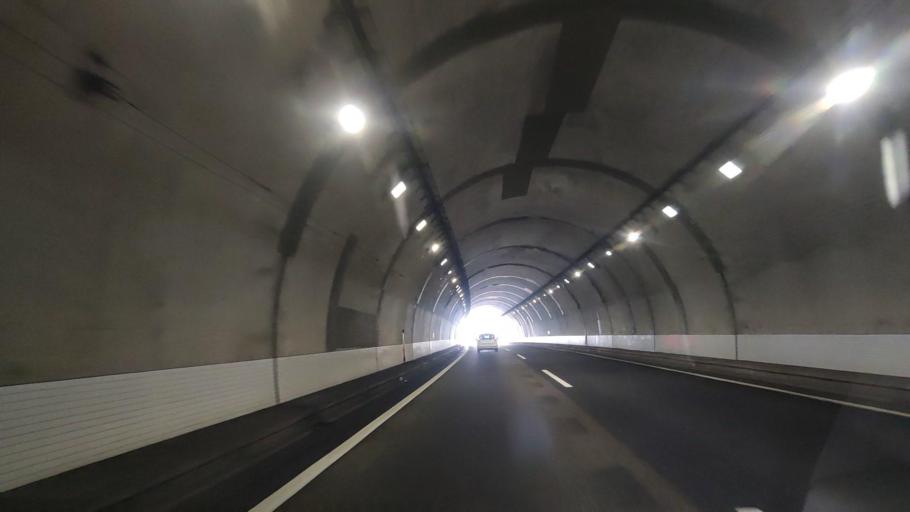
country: JP
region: Niigata
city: Joetsu
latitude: 37.1035
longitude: 138.2207
